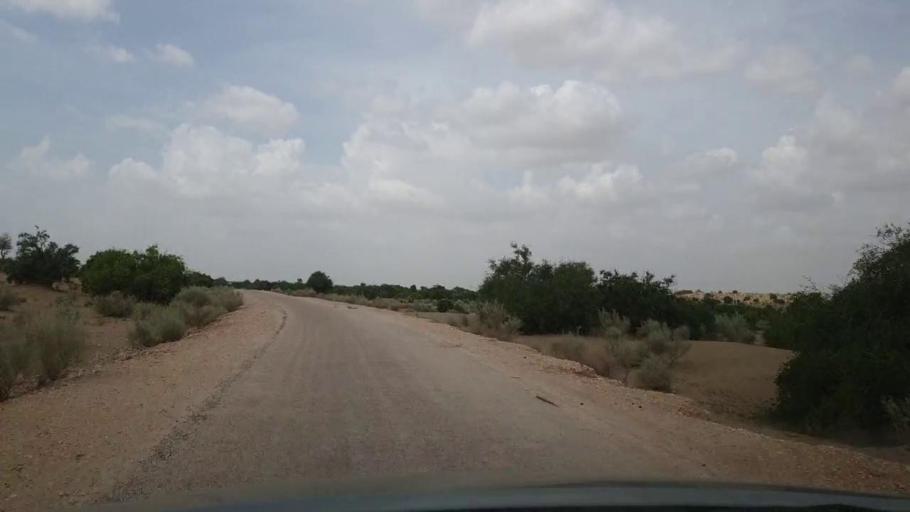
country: PK
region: Sindh
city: Kot Diji
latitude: 27.2161
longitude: 69.0836
